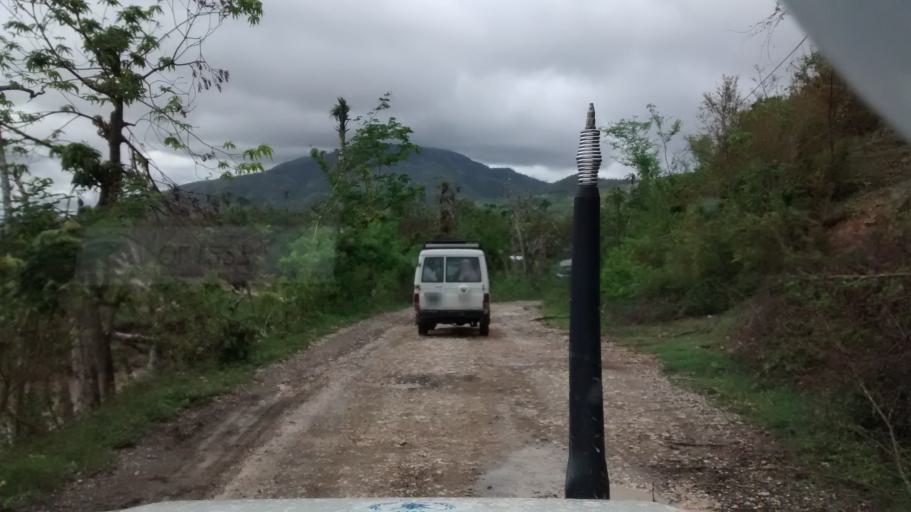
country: HT
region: Grandans
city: Moron
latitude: 18.5986
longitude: -74.1865
